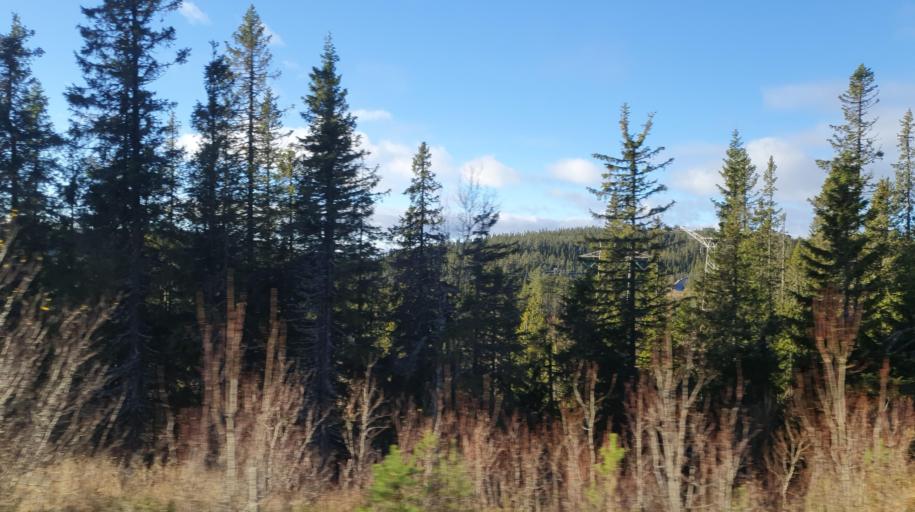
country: NO
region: Buskerud
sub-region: Krodsherad
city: Noresund
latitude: 60.2182
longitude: 9.5357
